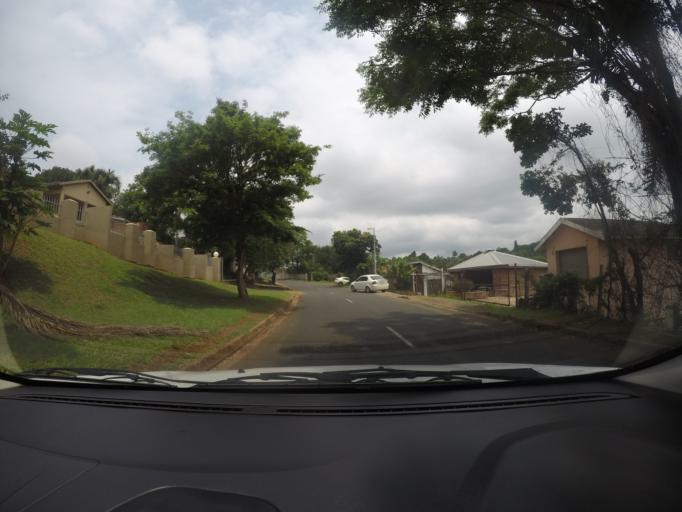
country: ZA
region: KwaZulu-Natal
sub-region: uThungulu District Municipality
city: Empangeni
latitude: -28.7517
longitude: 31.8892
